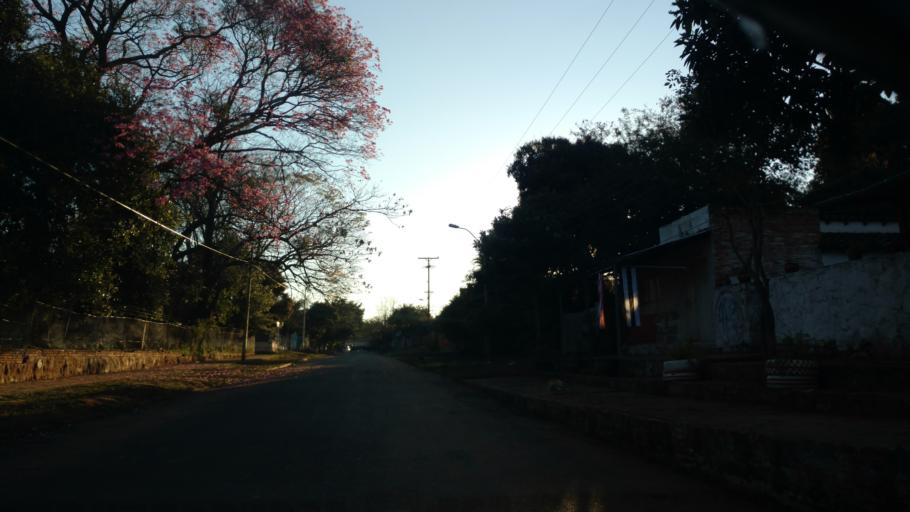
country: PY
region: Paraguari
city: Yaguaron
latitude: -25.5651
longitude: -57.2872
